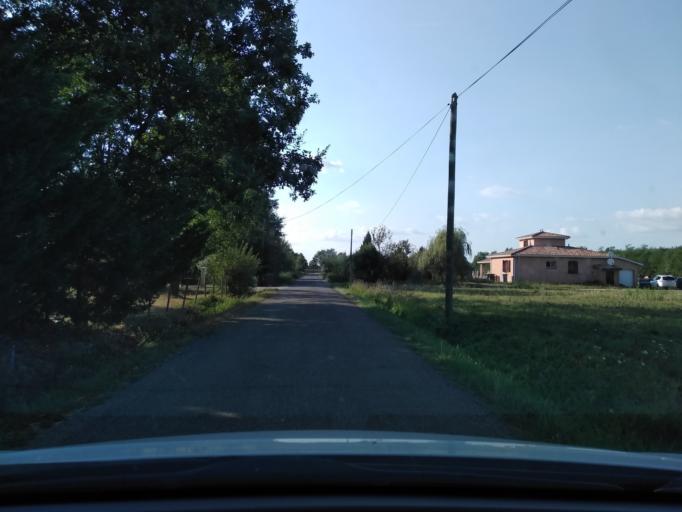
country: FR
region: Midi-Pyrenees
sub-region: Departement du Tarn-et-Garonne
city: Montech
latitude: 43.9668
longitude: 1.2455
